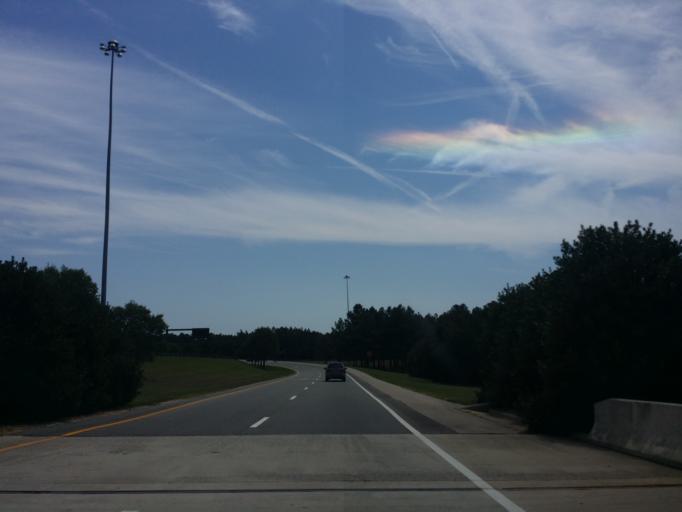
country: US
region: North Carolina
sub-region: Wake County
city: Morrisville
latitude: 35.8647
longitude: -78.8048
